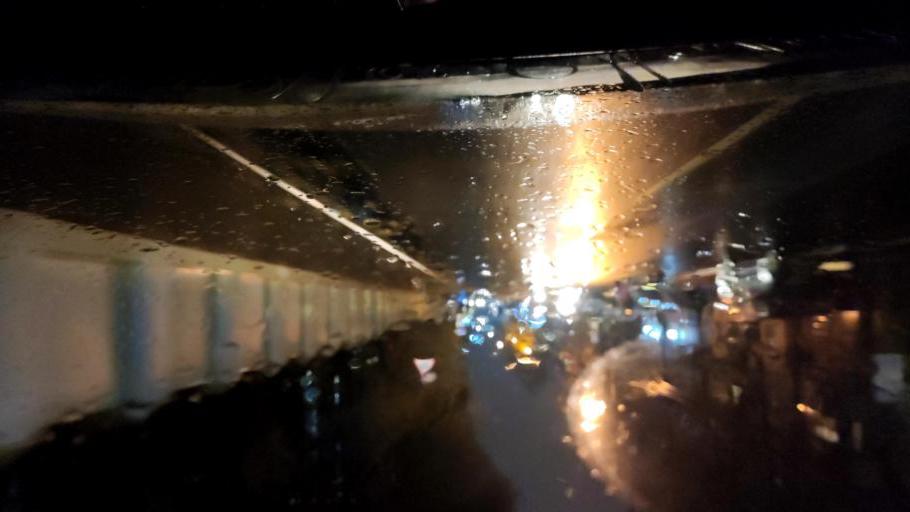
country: RU
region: Voronezj
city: Voronezh
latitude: 51.6583
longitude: 39.2096
